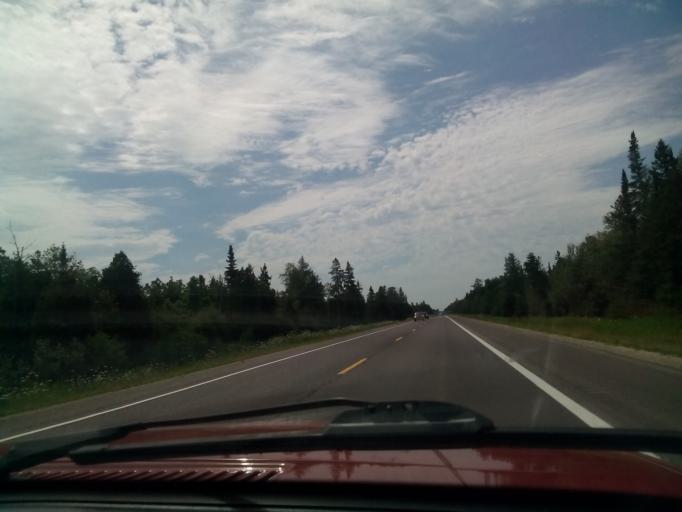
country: US
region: Michigan
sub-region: Schoolcraft County
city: Manistique
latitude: 46.0352
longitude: -85.9771
